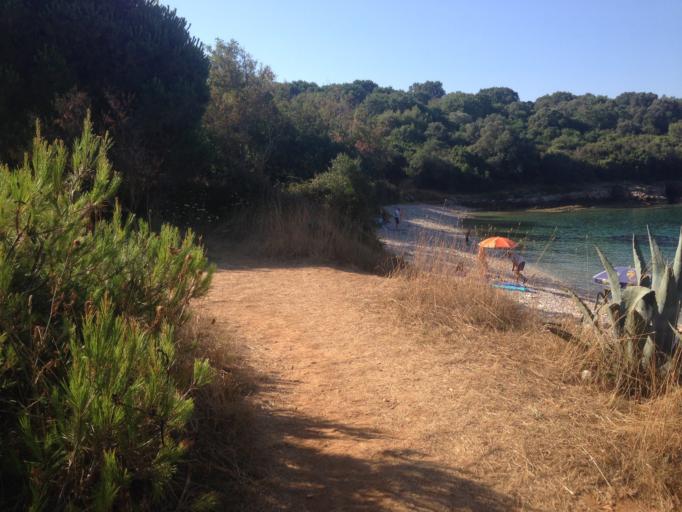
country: HR
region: Istarska
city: Medulin
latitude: 44.7866
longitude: 13.9070
